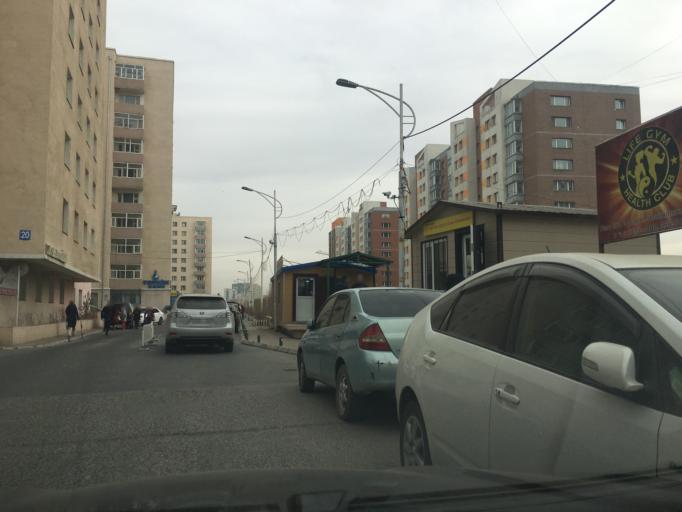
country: MN
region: Ulaanbaatar
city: Ulaanbaatar
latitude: 47.9031
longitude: 106.8871
